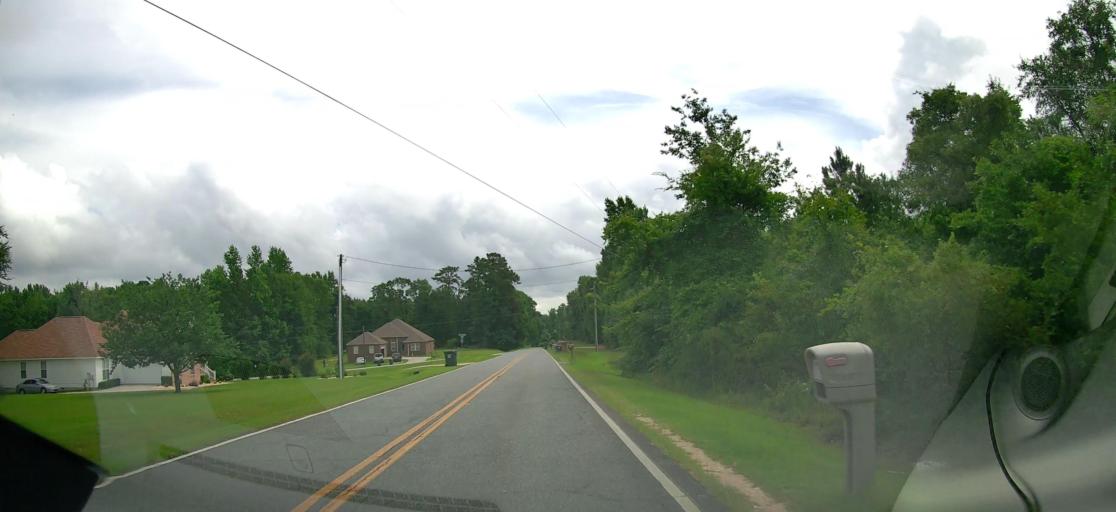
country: US
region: Georgia
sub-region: Bibb County
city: West Point
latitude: 32.7934
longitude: -83.7886
